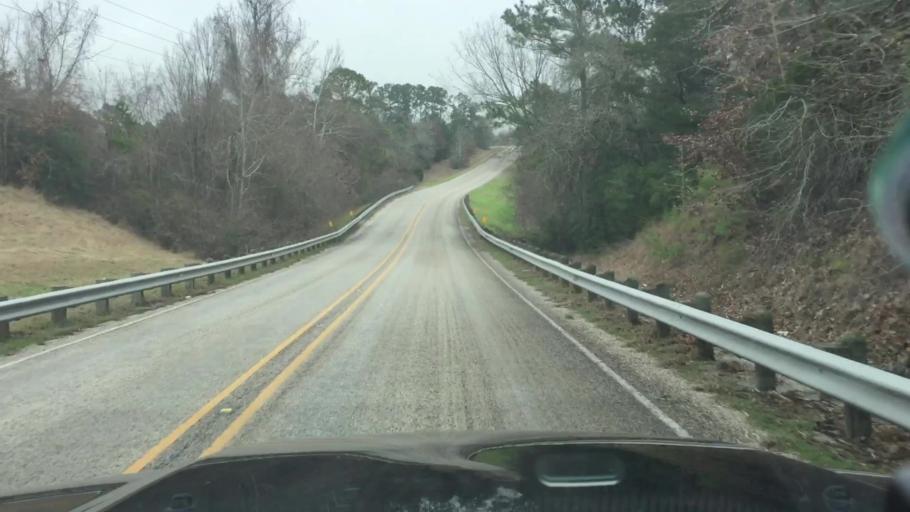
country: US
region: Texas
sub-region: Fayette County
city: La Grange
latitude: 30.0020
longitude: -96.8978
